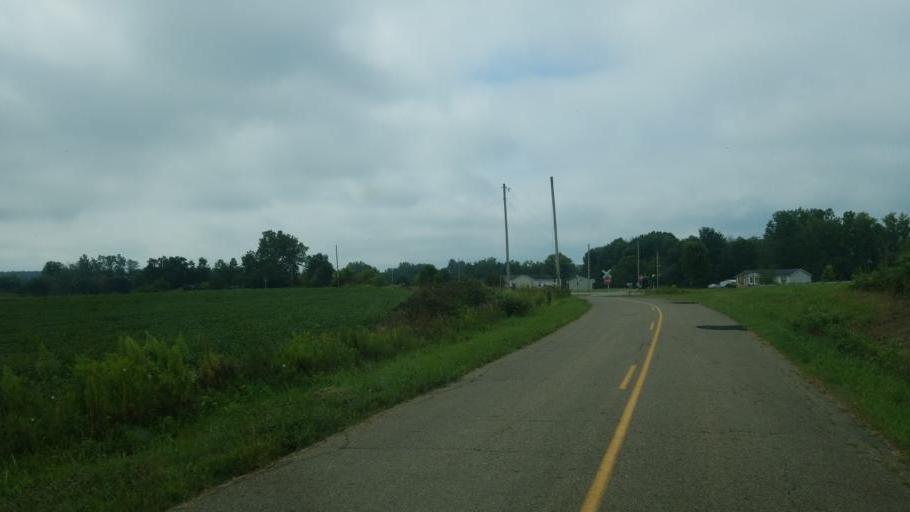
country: US
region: Ohio
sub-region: Licking County
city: Utica
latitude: 40.2734
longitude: -82.4492
